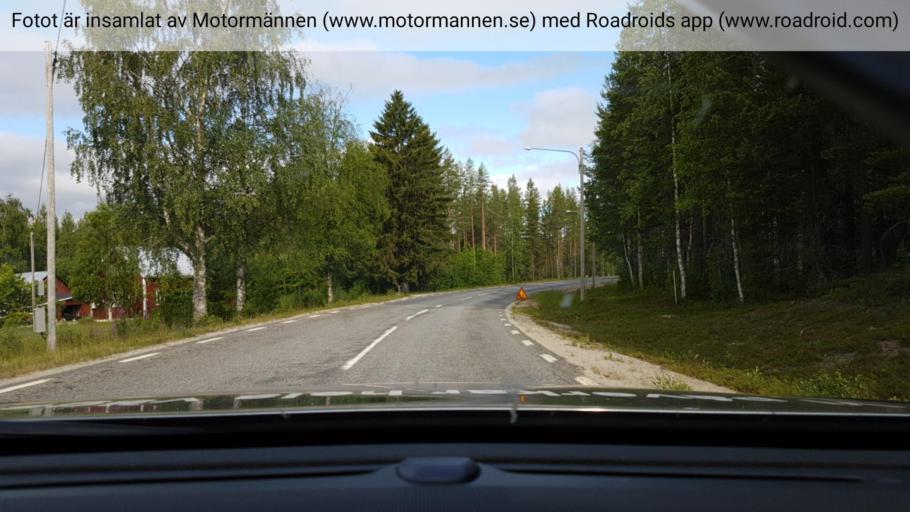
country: SE
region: Vaesterbotten
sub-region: Norsjo Kommun
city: Norsjoe
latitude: 64.7167
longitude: 19.1386
